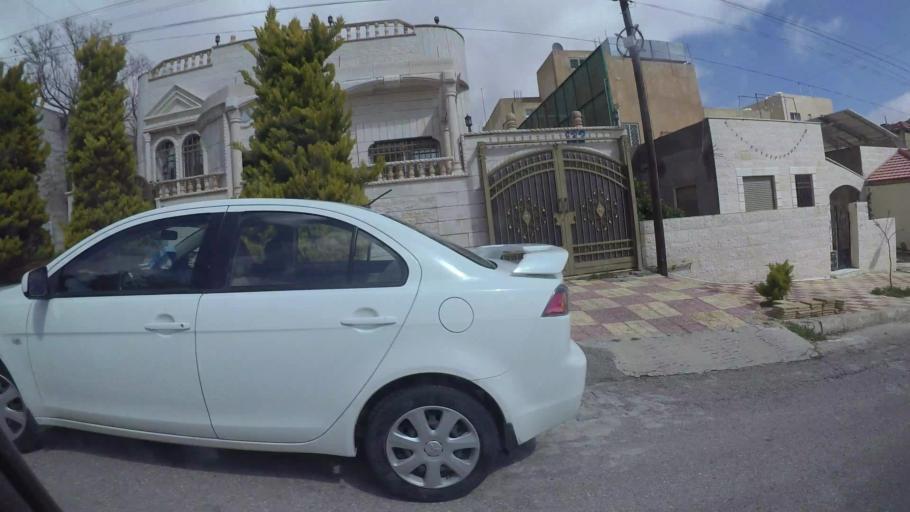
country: JO
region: Amman
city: Al Jubayhah
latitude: 32.0638
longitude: 35.8783
